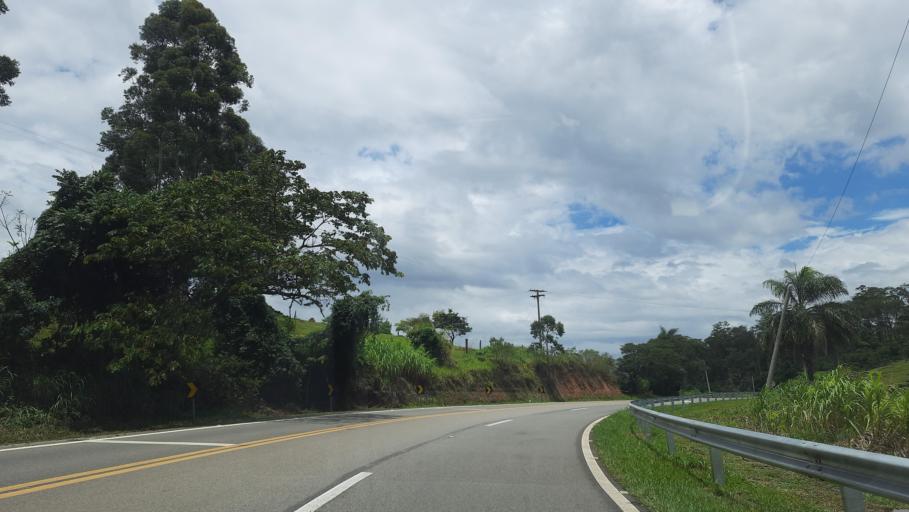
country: BR
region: Sao Paulo
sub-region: Vargem Grande Do Sul
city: Vargem Grande do Sul
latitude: -21.7992
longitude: -46.8186
